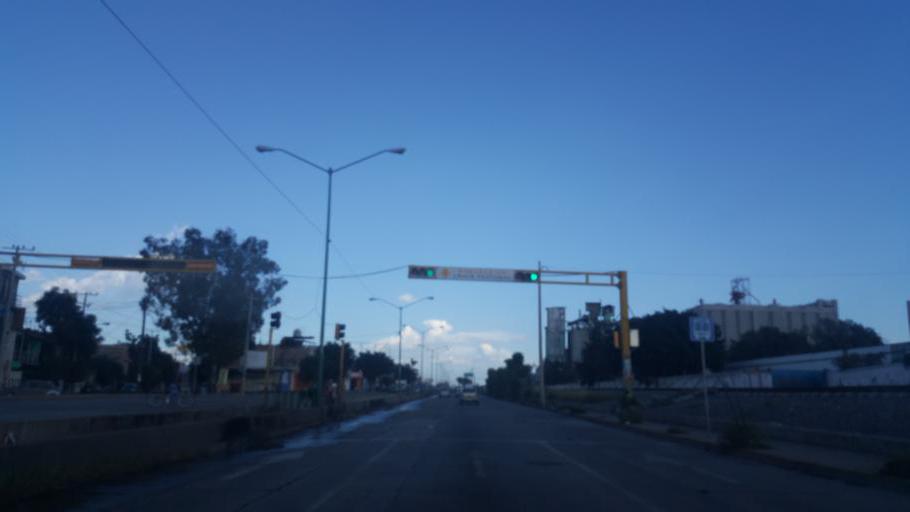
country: MX
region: Guanajuato
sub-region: Leon
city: San Jose de Duran (Los Troncoso)
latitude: 21.0864
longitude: -101.6699
